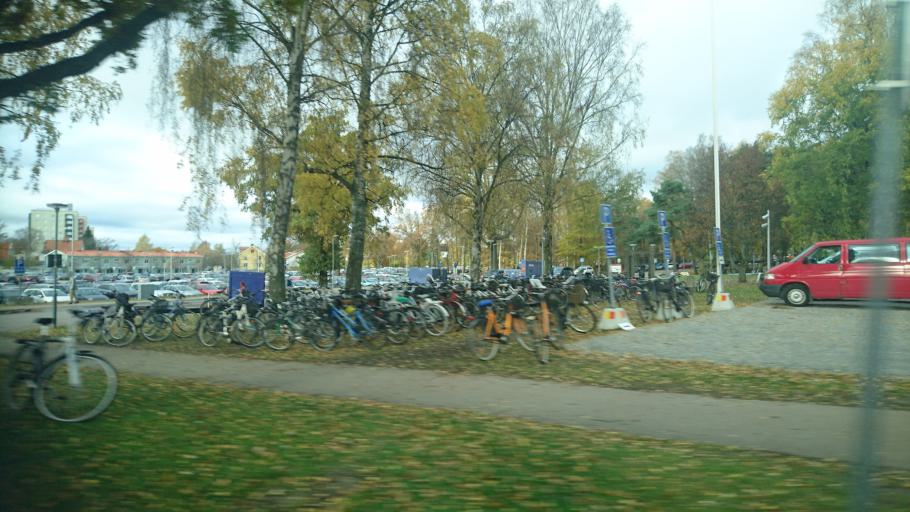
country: SE
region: Vaestmanland
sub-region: Vasteras
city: Vasteras
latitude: 59.6173
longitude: 16.5801
